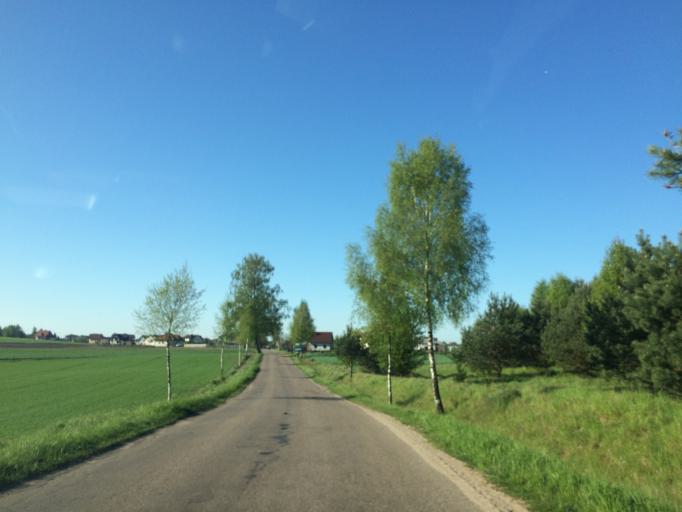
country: PL
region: Warmian-Masurian Voivodeship
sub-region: Powiat dzialdowski
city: Rybno
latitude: 53.3954
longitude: 19.9330
